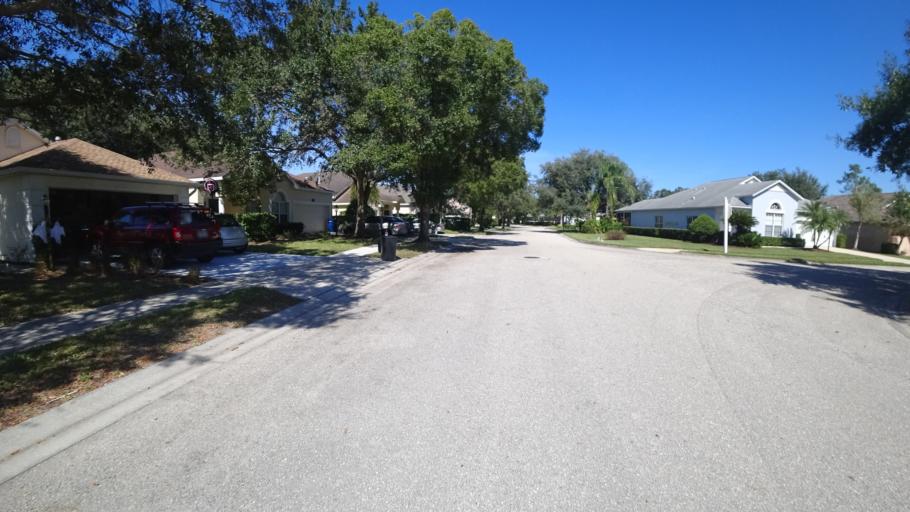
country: US
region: Florida
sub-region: Sarasota County
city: The Meadows
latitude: 27.4292
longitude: -82.4195
